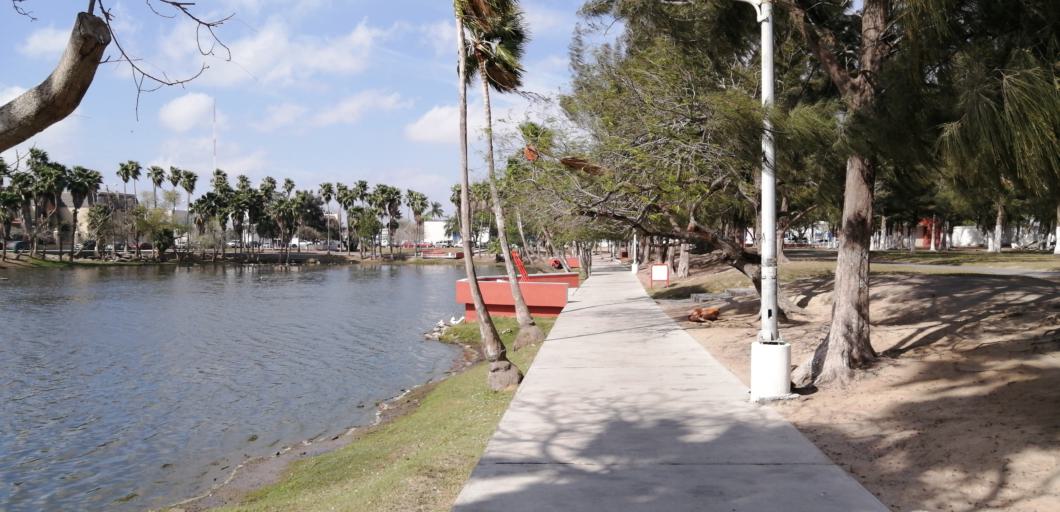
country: MX
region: Tamaulipas
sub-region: Matamoros
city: Heroica Matamoros
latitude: 25.8685
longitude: -97.4942
